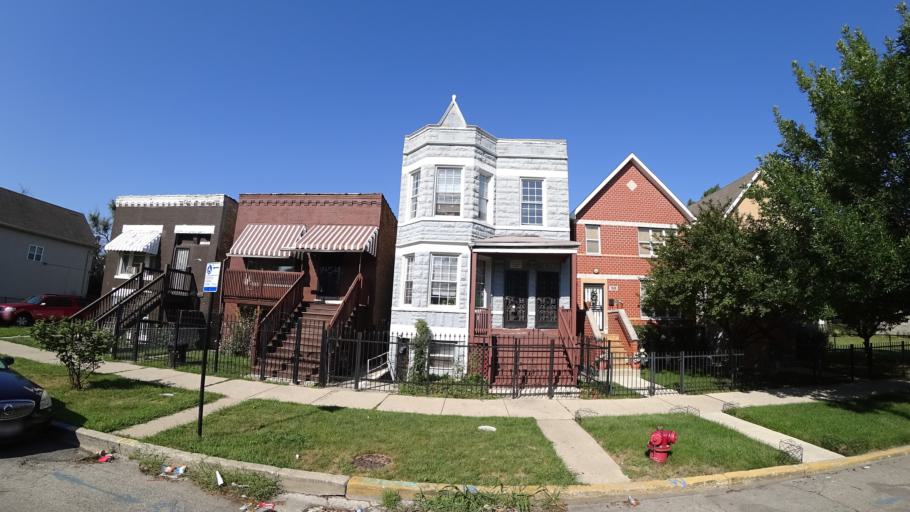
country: US
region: Illinois
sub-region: Cook County
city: Cicero
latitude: 41.8580
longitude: -87.7189
